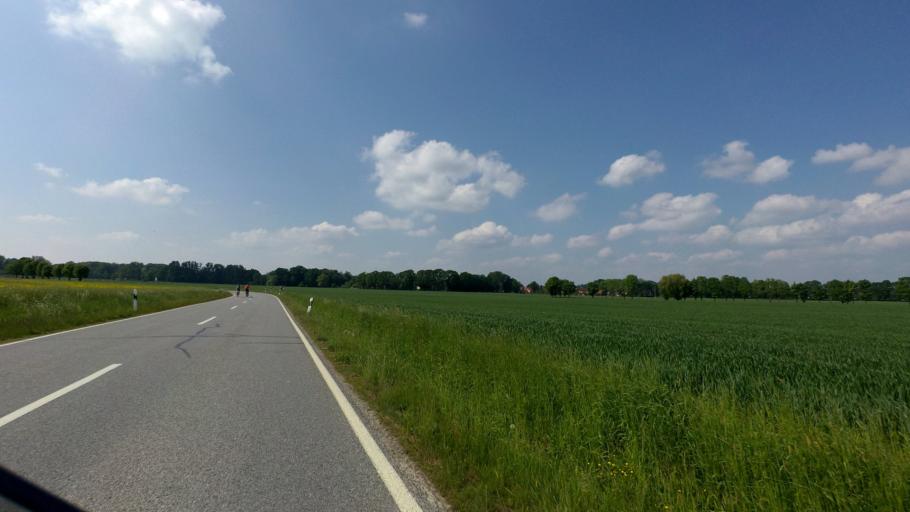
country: DE
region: Saxony
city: Guttau
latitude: 51.2180
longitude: 14.5976
